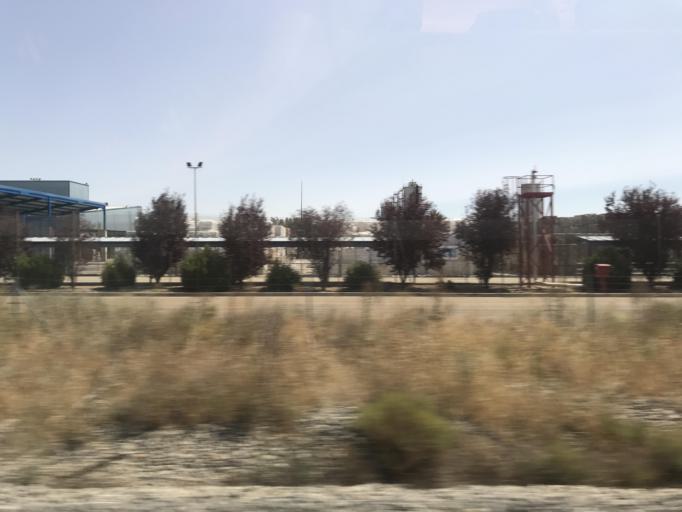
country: ES
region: Castille and Leon
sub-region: Provincia de Palencia
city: Duenas
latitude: 41.8398
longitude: -4.5603
